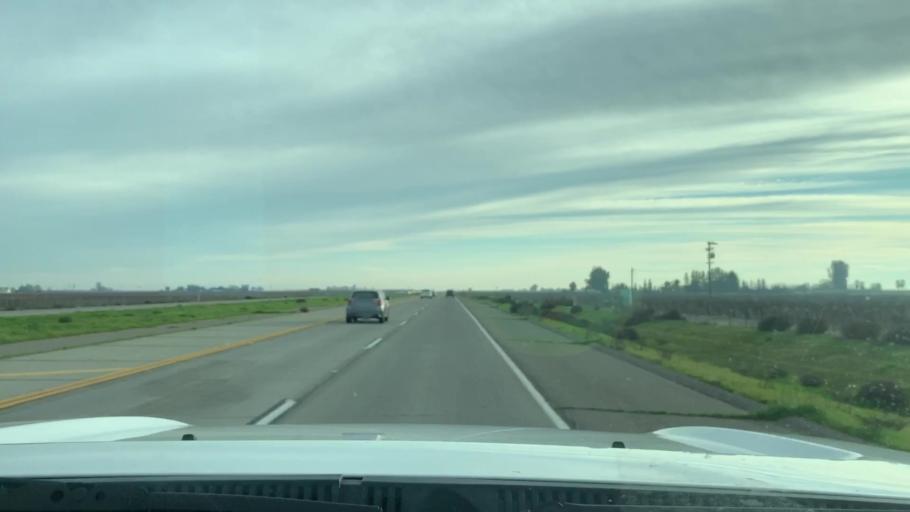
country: US
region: California
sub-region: Fresno County
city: Caruthers
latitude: 36.5610
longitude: -119.7863
